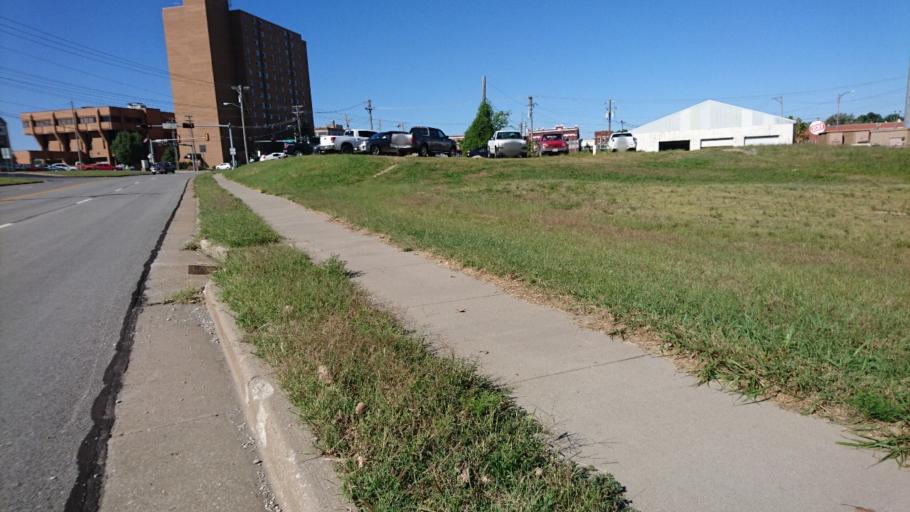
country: US
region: Missouri
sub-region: Jasper County
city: Joplin
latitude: 37.0903
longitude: -94.5110
